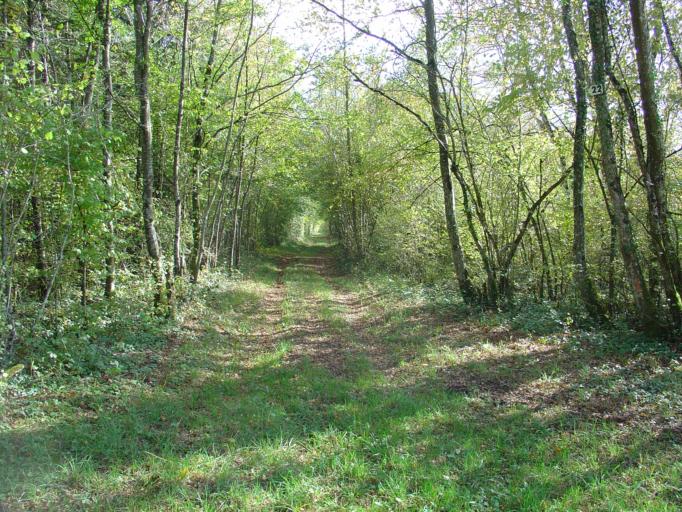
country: FR
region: Lorraine
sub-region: Departement de Meurthe-et-Moselle
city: Colombey-les-Belles
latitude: 48.5542
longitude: 5.9453
